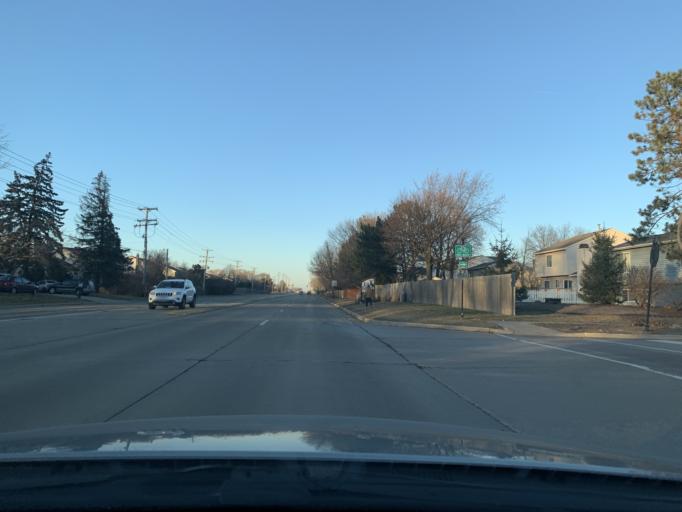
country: US
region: Illinois
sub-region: DuPage County
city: Roselle
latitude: 42.0018
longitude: -88.0605
